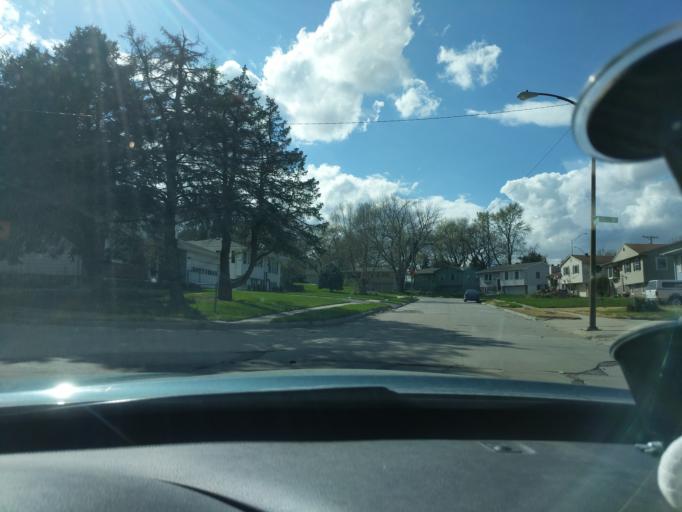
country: US
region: Nebraska
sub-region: Douglas County
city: Ralston
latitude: 41.2332
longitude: -96.0958
